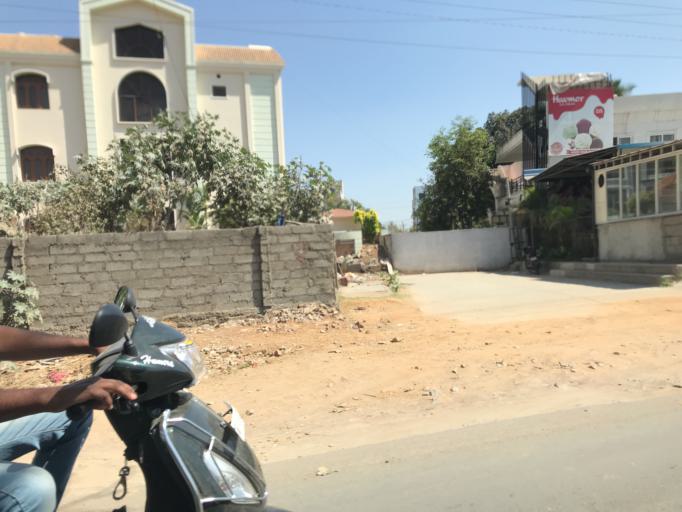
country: IN
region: Telangana
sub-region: Medak
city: Serilingampalle
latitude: 17.4728
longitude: 78.3277
